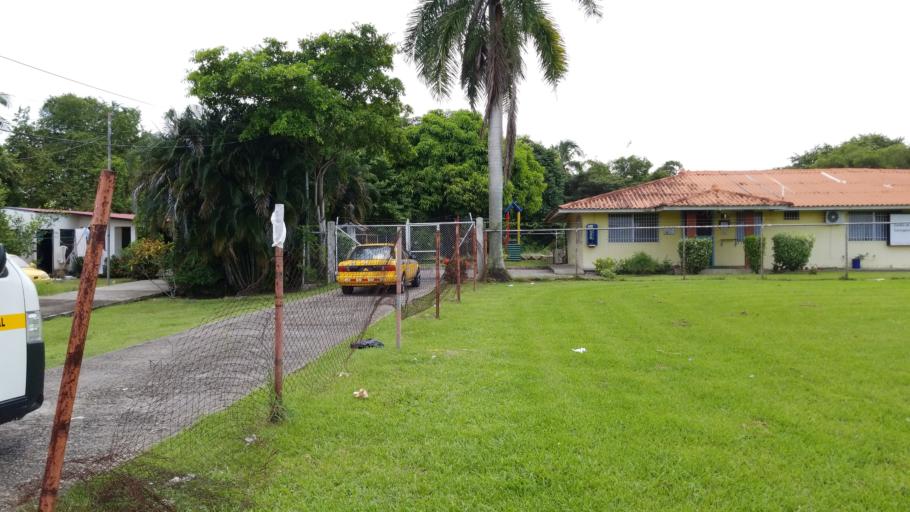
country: PA
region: Panama
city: San Miguelito
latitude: 9.0421
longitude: -79.4357
